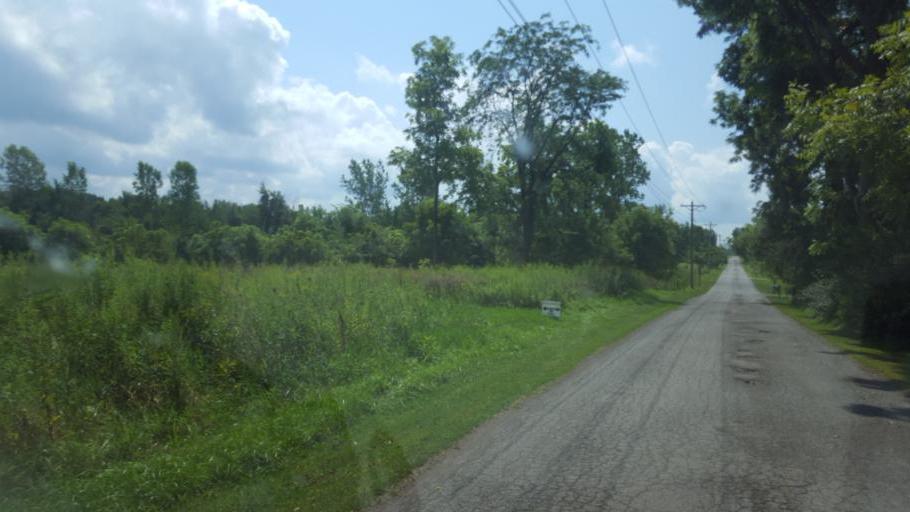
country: US
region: Ohio
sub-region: Knox County
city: Fredericktown
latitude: 40.4297
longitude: -82.6498
